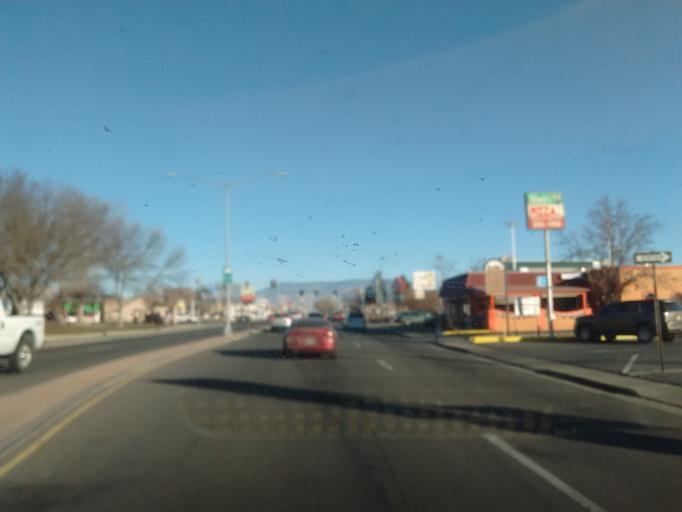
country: US
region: Colorado
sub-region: Mesa County
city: Grand Junction
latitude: 39.0774
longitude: -108.5537
